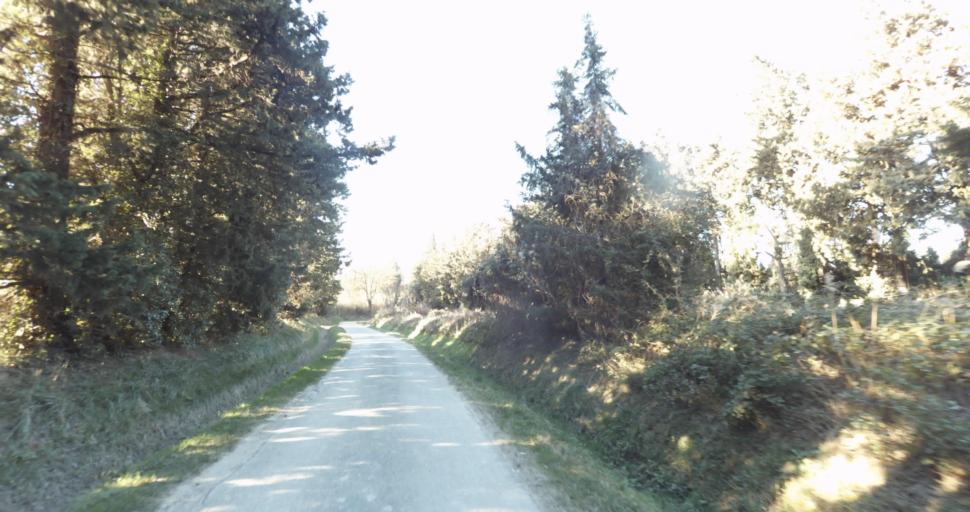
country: FR
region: Provence-Alpes-Cote d'Azur
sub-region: Departement des Bouches-du-Rhone
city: Barbentane
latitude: 43.9070
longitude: 4.7480
